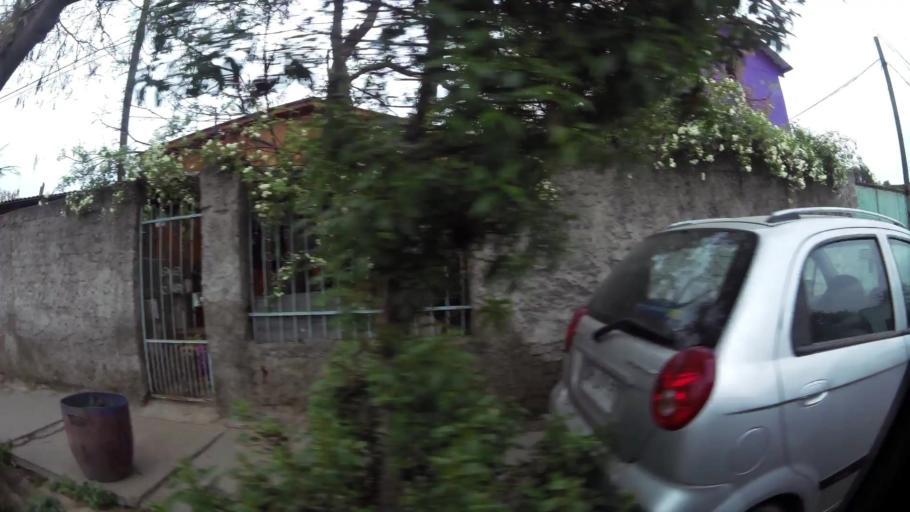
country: CL
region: Santiago Metropolitan
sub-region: Provincia de Santiago
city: Lo Prado
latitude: -33.5063
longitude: -70.7604
